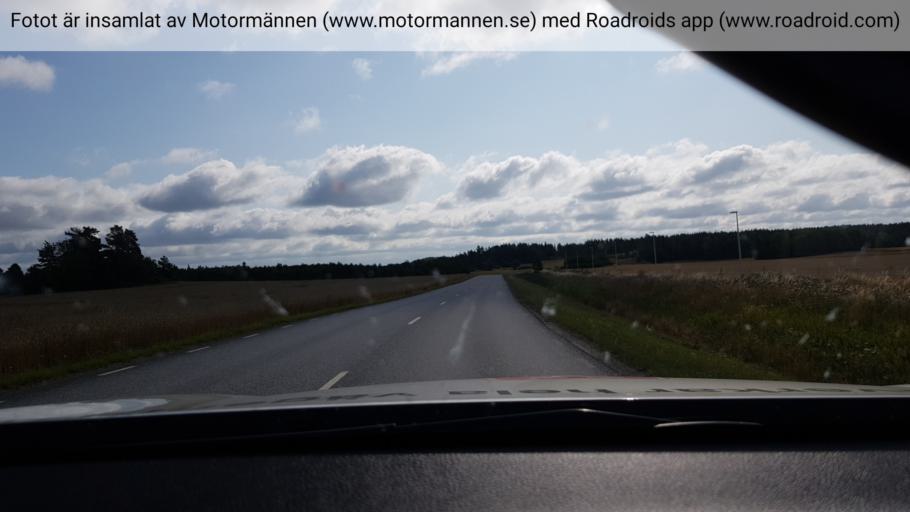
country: SE
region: Uppsala
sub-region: Uppsala Kommun
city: Alsike
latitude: 59.7162
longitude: 17.7409
